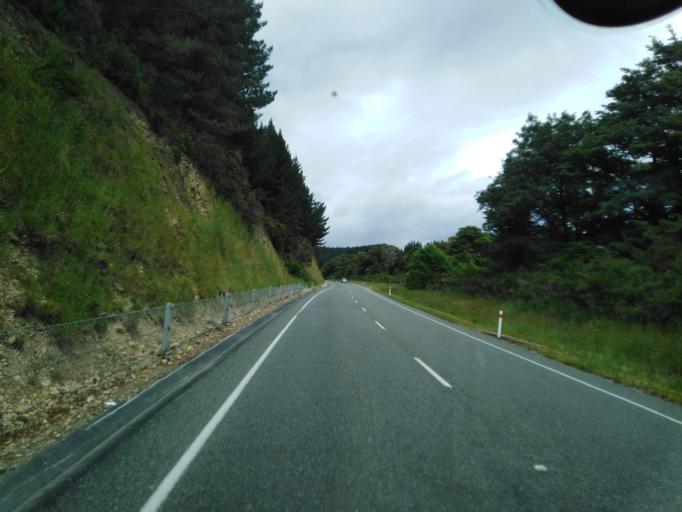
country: NZ
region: Tasman
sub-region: Tasman District
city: Wakefield
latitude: -41.4749
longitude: 172.9352
